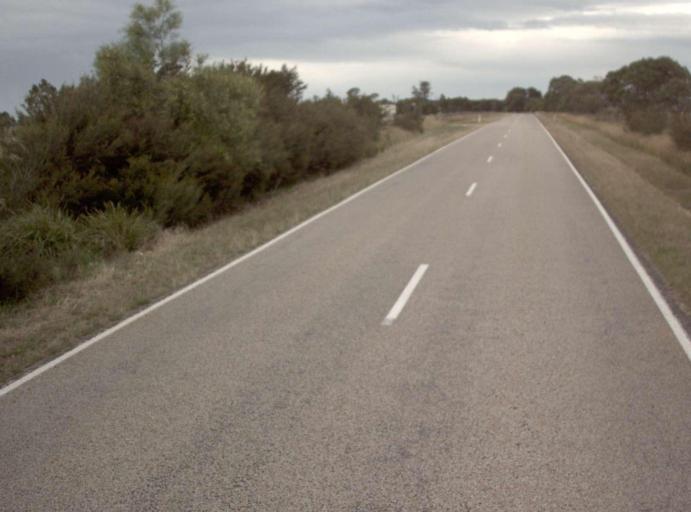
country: AU
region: Victoria
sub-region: East Gippsland
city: Bairnsdale
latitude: -37.9561
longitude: 147.5048
